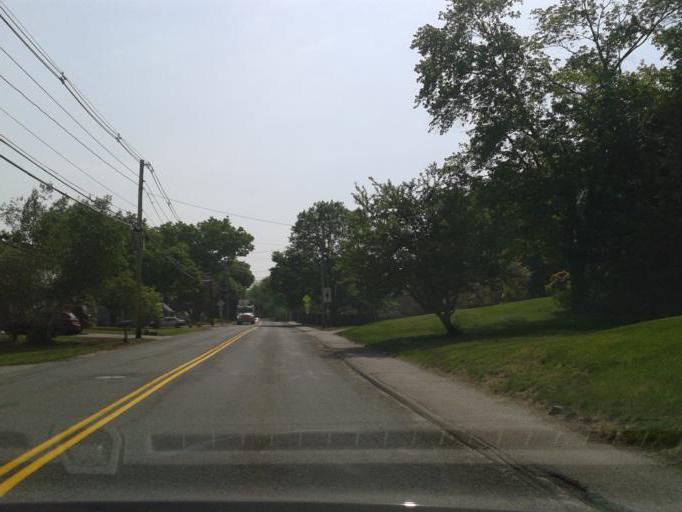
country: US
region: Massachusetts
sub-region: Worcester County
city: Westborough
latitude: 42.2709
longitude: -71.6283
